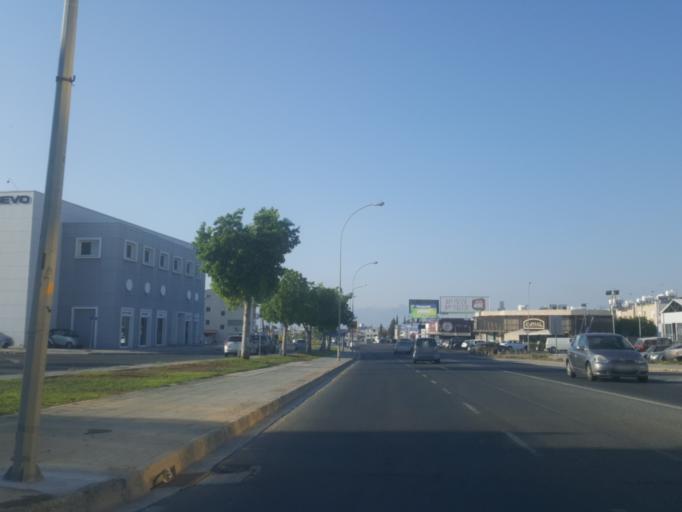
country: CY
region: Lefkosia
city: Nicosia
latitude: 35.1320
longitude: 33.3576
